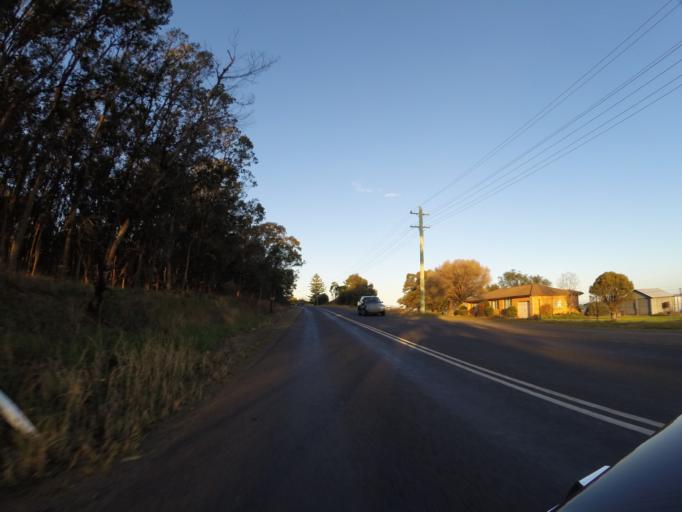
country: AU
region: New South Wales
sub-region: Camden
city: Cobbitty
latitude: -34.0197
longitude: 150.6687
